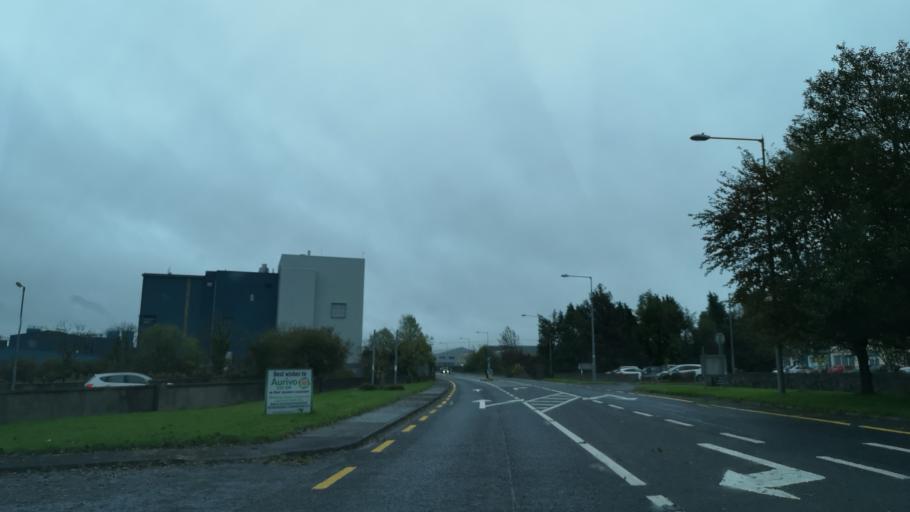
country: IE
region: Connaught
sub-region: Roscommon
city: Ballaghaderreen
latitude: 53.8986
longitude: -8.5727
